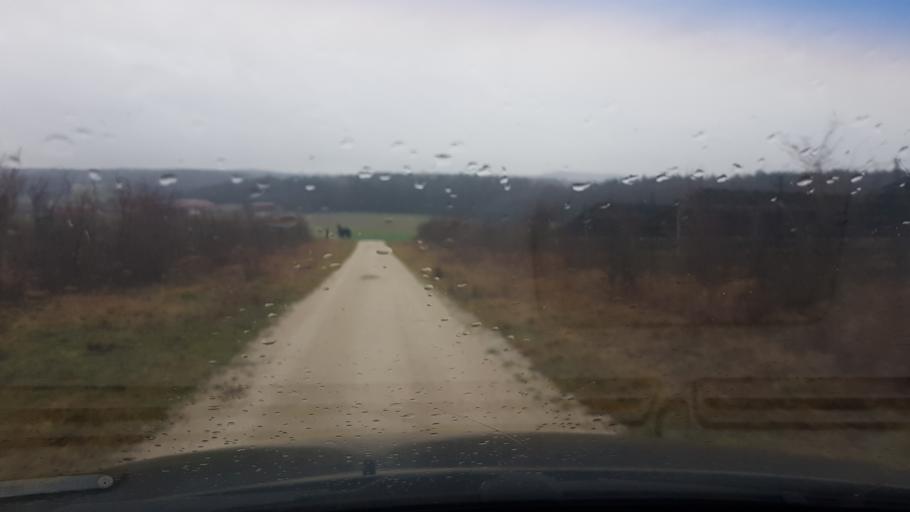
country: DE
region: Bavaria
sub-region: Upper Franconia
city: Zapfendorf
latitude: 50.0266
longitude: 10.9629
